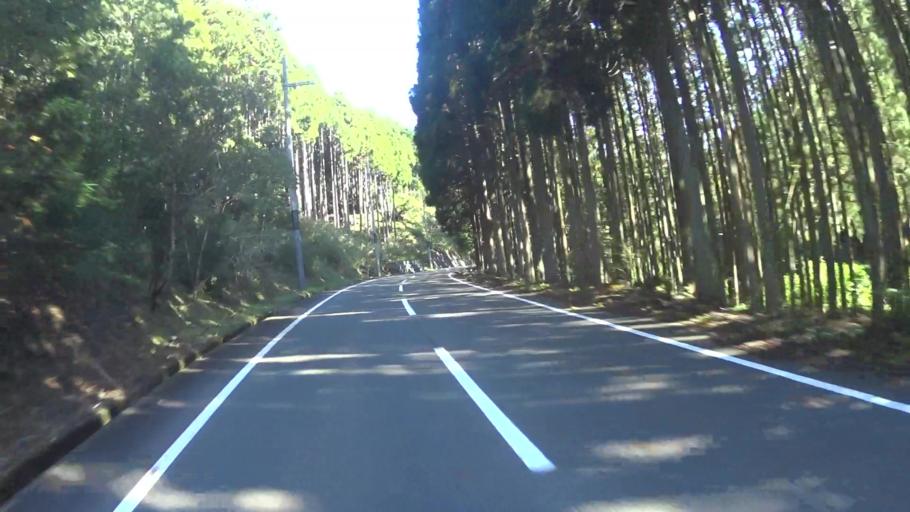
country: JP
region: Kyoto
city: Kameoka
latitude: 35.1165
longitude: 135.5673
